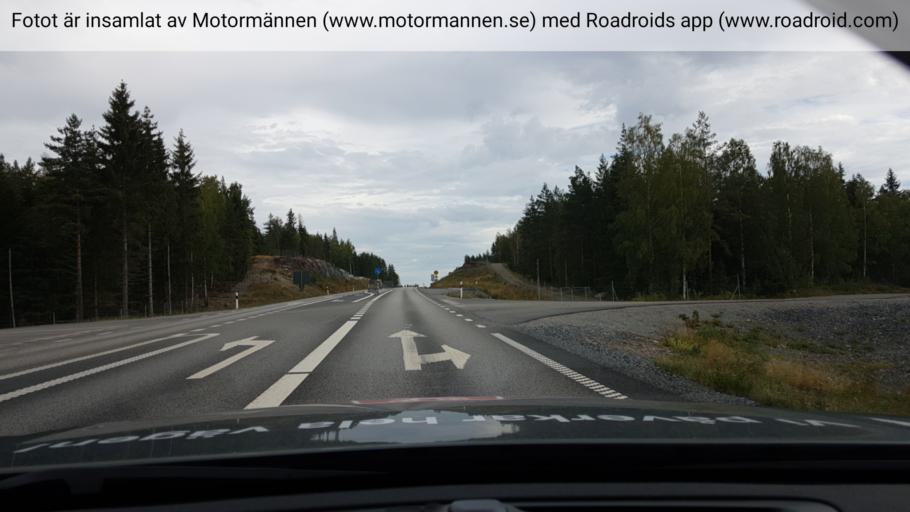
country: SE
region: Uppsala
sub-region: Heby Kommun
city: Heby
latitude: 60.0157
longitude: 16.8559
